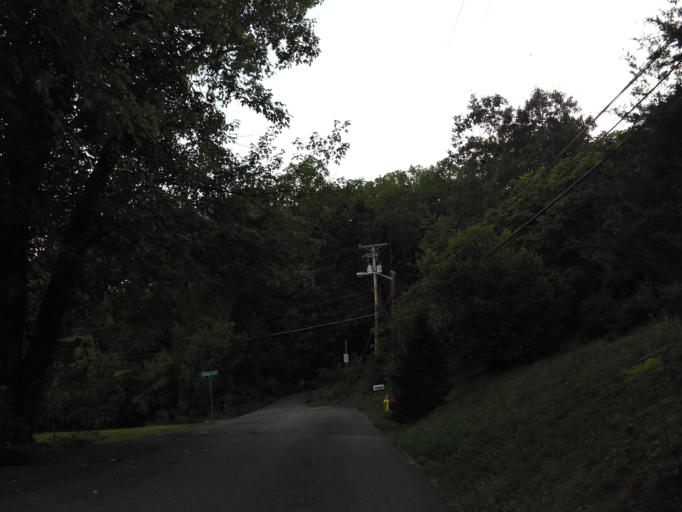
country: US
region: Tennessee
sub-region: Knox County
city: Knoxville
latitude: 36.0020
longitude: -83.9411
